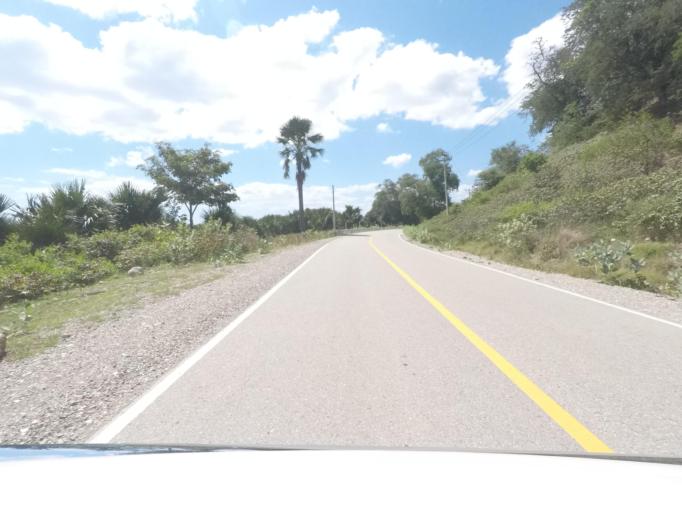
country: TL
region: Lautem
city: Lospalos
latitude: -8.4153
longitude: 126.7997
